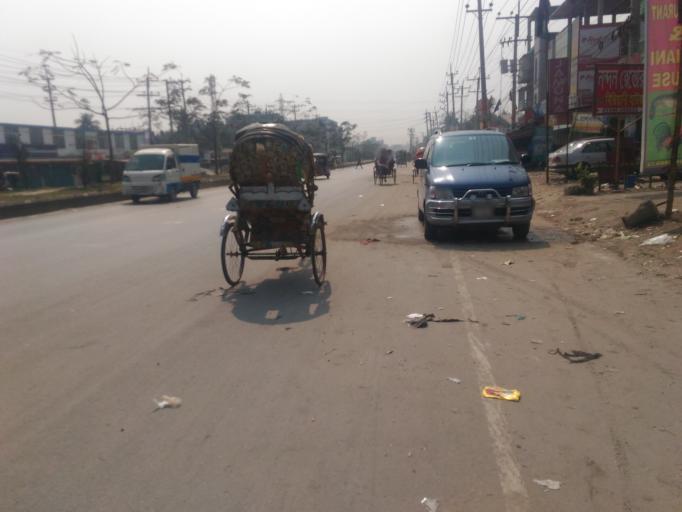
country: BD
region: Dhaka
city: Tungi
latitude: 24.0003
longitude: 90.3826
